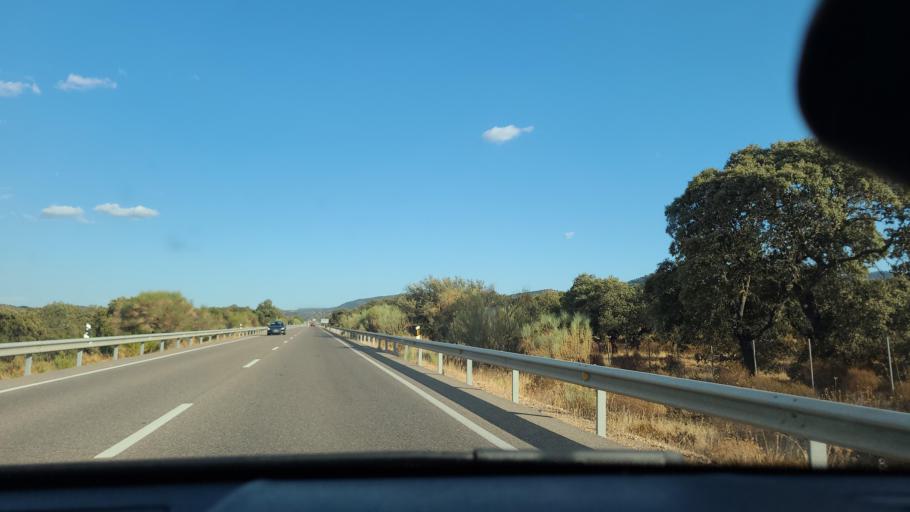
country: ES
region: Andalusia
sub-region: Province of Cordoba
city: Belmez
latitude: 38.2210
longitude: -5.1527
